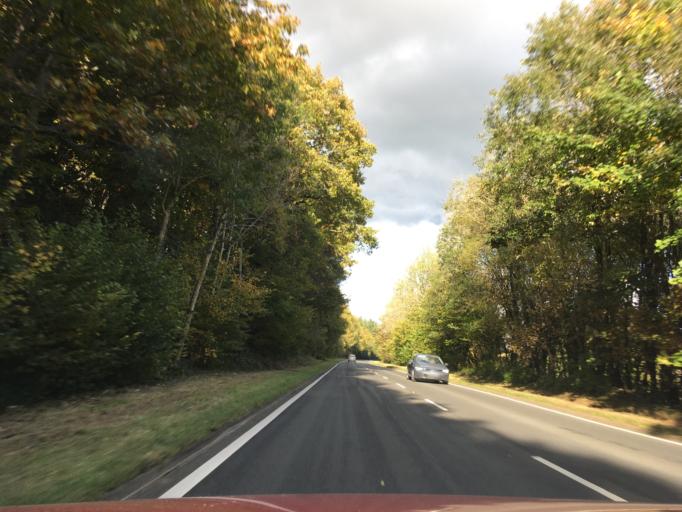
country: GB
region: Wales
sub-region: Sir Powys
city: Brecon
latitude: 51.9001
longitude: -3.4904
